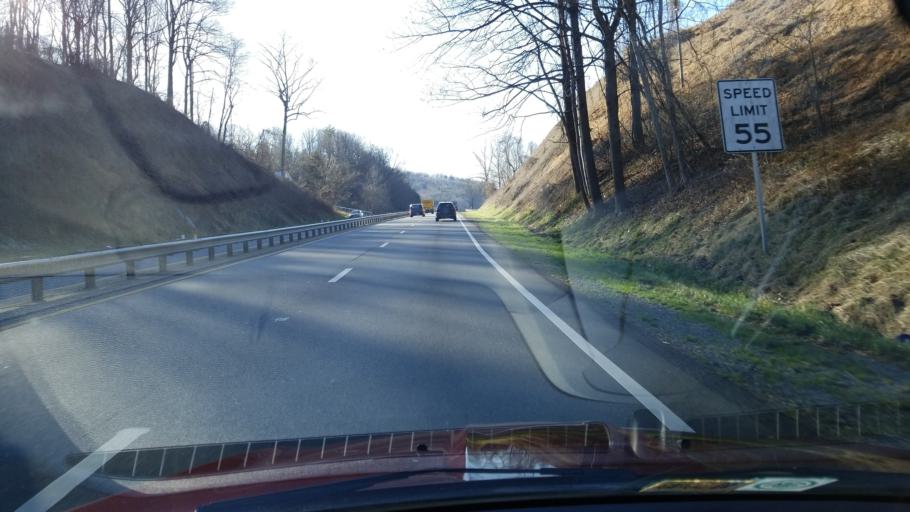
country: US
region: Virginia
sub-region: Roanoke County
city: Narrows
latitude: 37.1097
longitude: -79.9463
